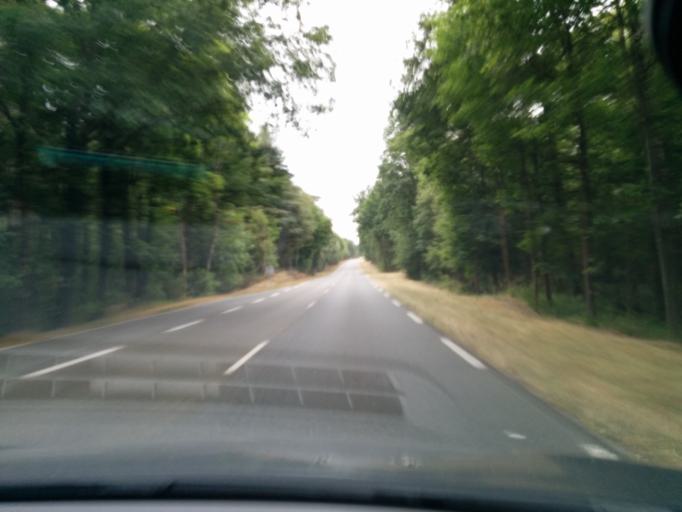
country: FR
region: Ile-de-France
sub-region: Departement des Yvelines
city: Gazeran
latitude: 48.6766
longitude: 1.7875
